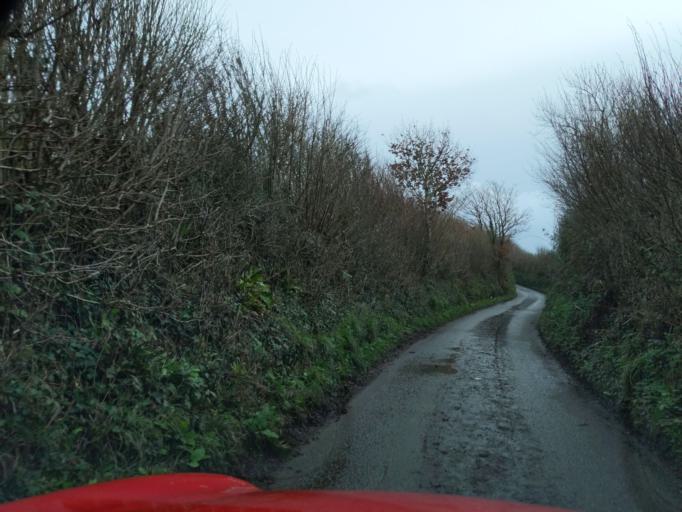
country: GB
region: England
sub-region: Cornwall
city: Duloe
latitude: 50.3552
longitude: -4.5160
